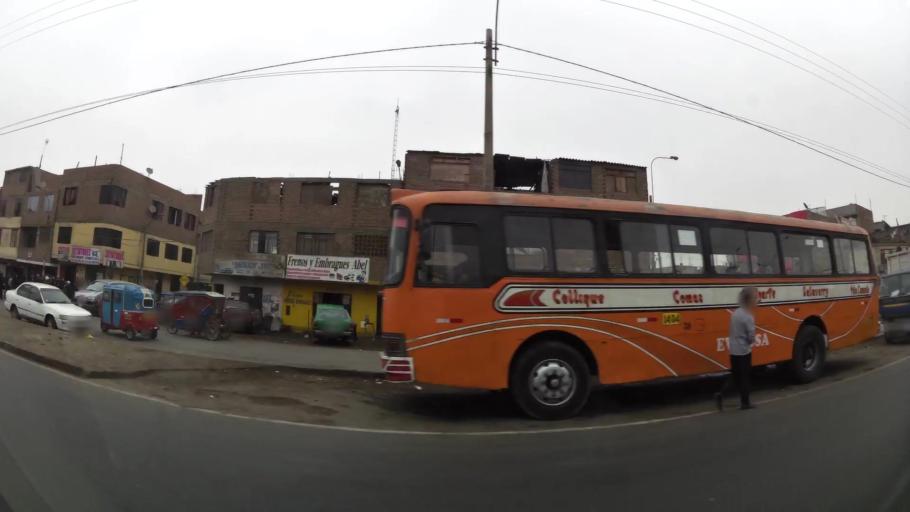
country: PE
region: Lima
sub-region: Lima
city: Urb. Santo Domingo
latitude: -11.9281
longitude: -77.0431
